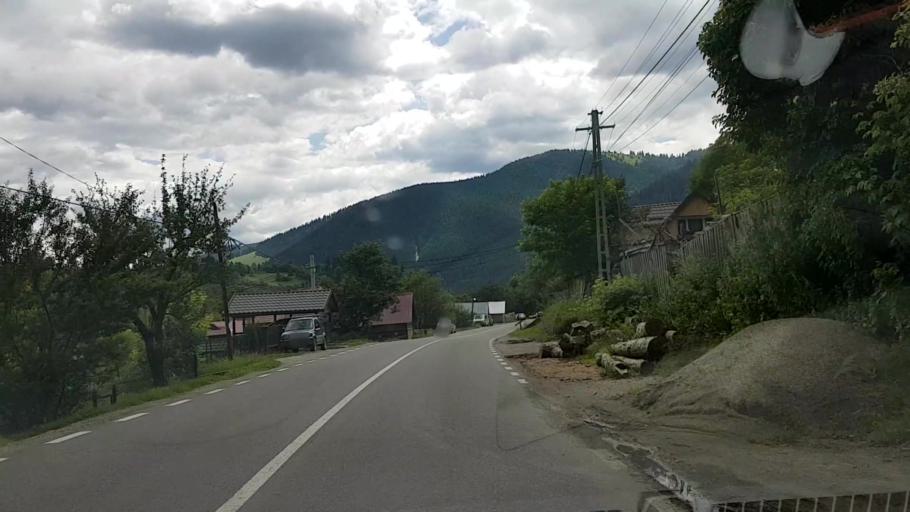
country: RO
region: Neamt
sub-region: Comuna Borca
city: Borca
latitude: 47.2133
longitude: 25.7559
